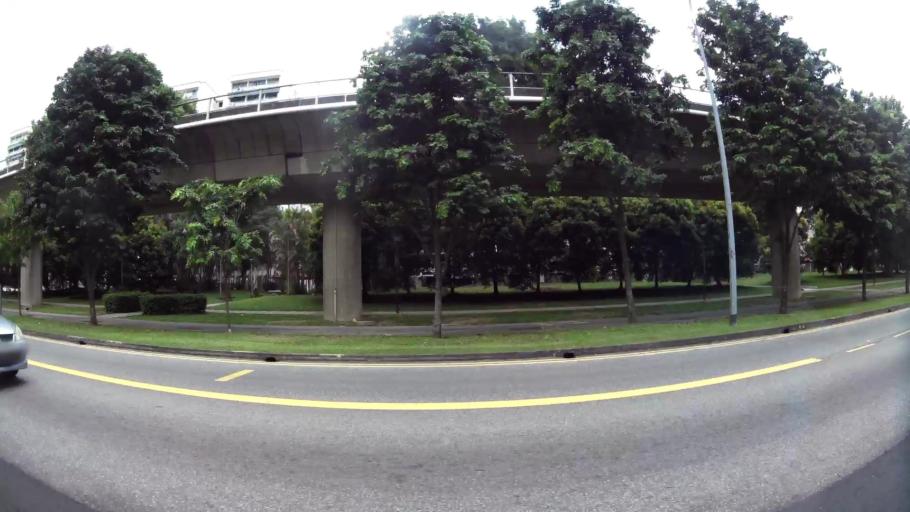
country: MY
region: Johor
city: Kampung Pasir Gudang Baru
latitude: 1.4219
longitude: 103.8348
